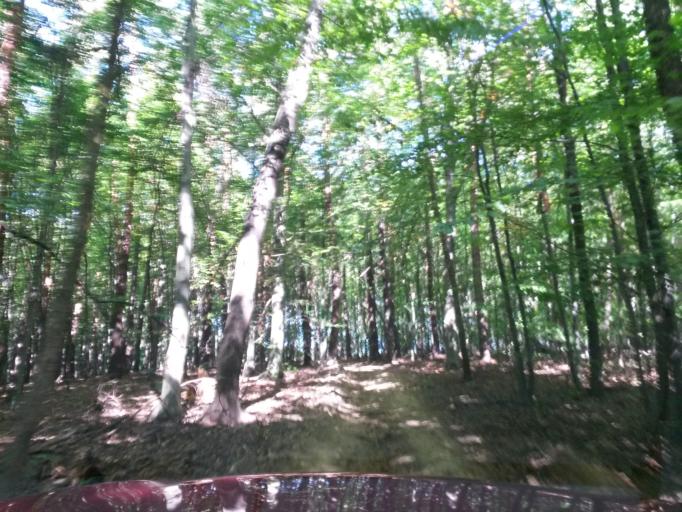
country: SK
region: Presovsky
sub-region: Okres Presov
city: Presov
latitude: 48.9824
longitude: 21.1474
